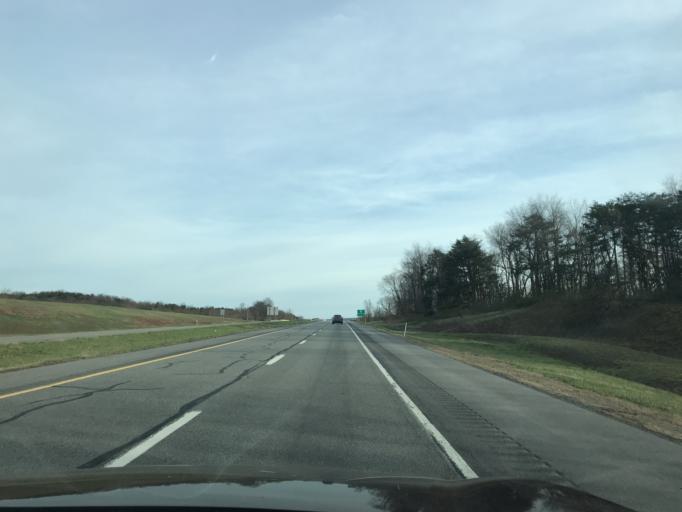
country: US
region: Pennsylvania
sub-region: Northumberland County
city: Milton
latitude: 41.0344
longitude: -76.8390
